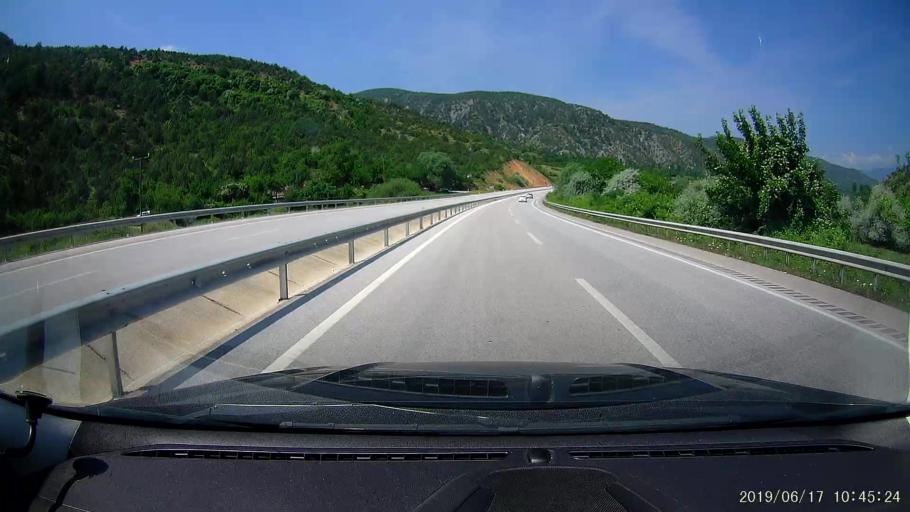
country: TR
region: Corum
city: Hacihamza
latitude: 41.0633
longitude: 34.4884
